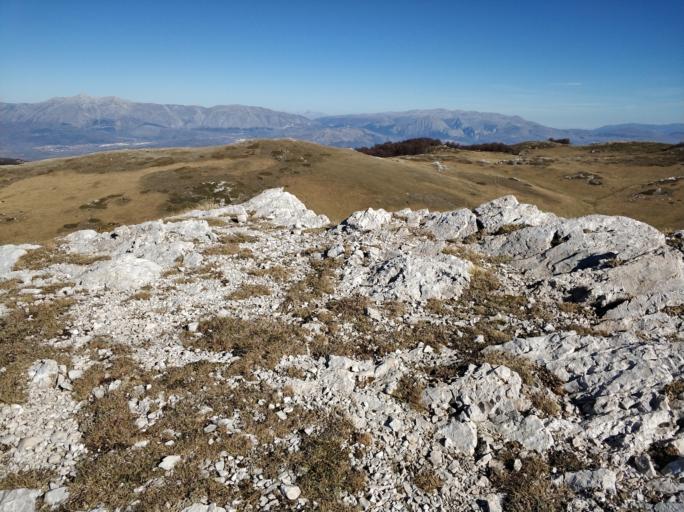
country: IT
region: Latium
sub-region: Provincia di Frosinone
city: Filettino
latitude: 41.9224
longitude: 13.3482
